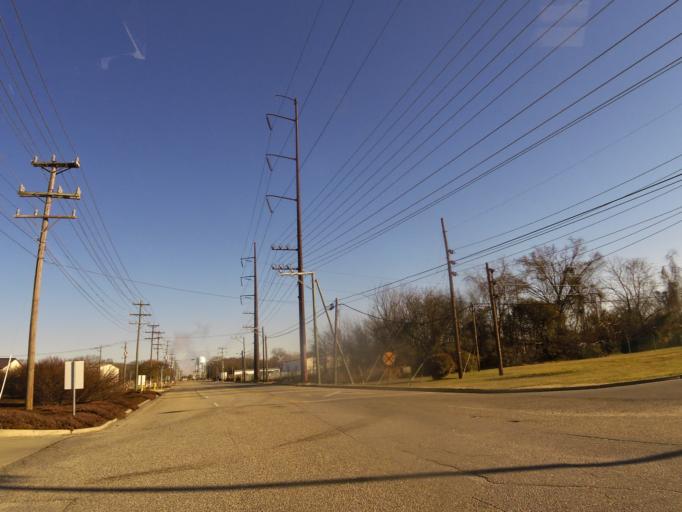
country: US
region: Virginia
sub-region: City of Hopewell
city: Hopewell
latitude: 37.2913
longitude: -77.2813
